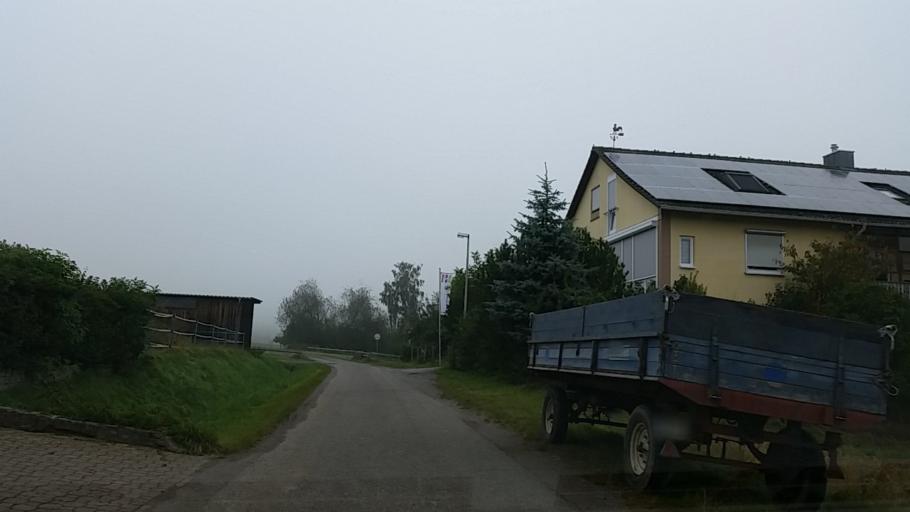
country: DE
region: Bavaria
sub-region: Regierungsbezirk Unterfranken
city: Himmelstadt
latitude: 49.9307
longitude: 9.8016
